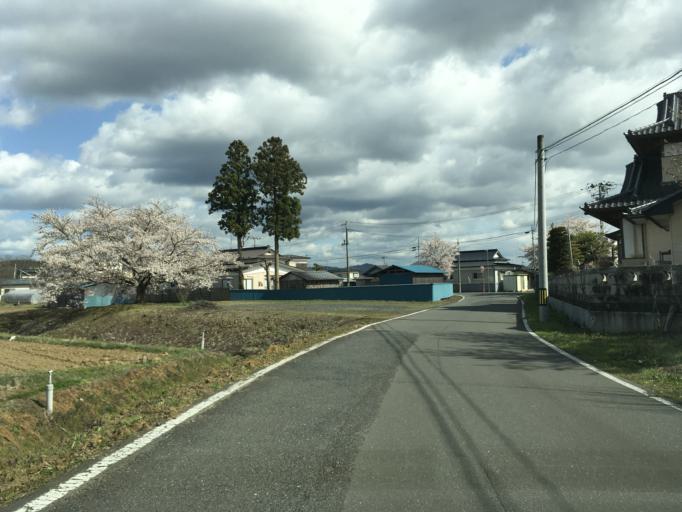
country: JP
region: Iwate
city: Ichinoseki
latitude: 38.7433
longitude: 141.2644
